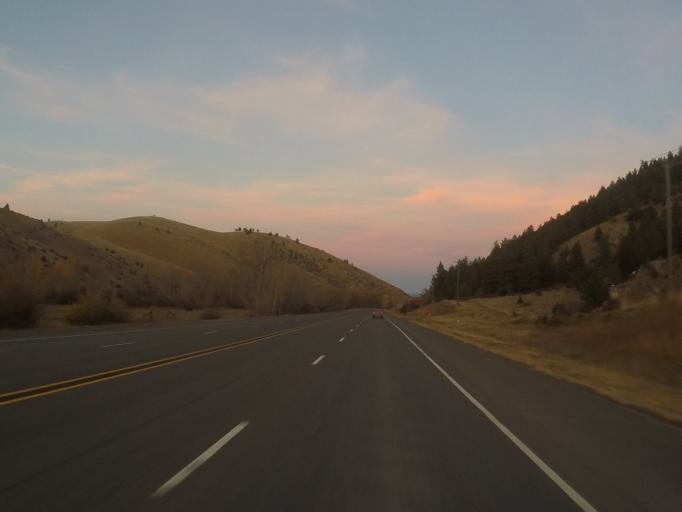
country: US
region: Montana
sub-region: Lewis and Clark County
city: Helena West Side
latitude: 46.5848
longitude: -112.1346
